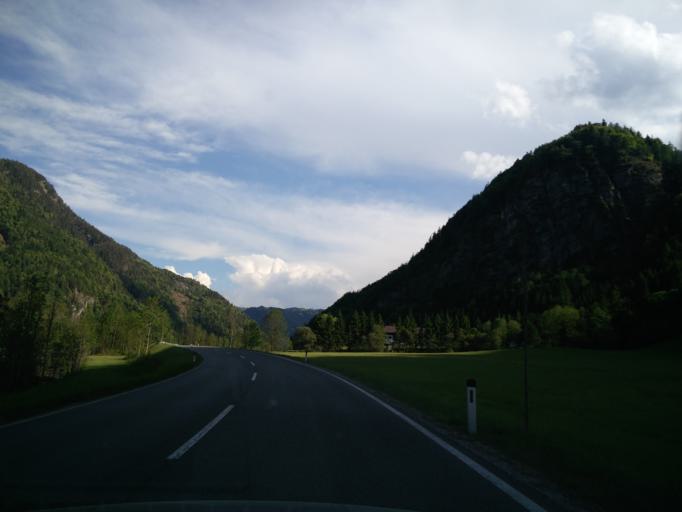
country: DE
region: Bavaria
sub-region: Upper Bavaria
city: Reit im Winkl
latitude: 47.6162
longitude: 12.4646
